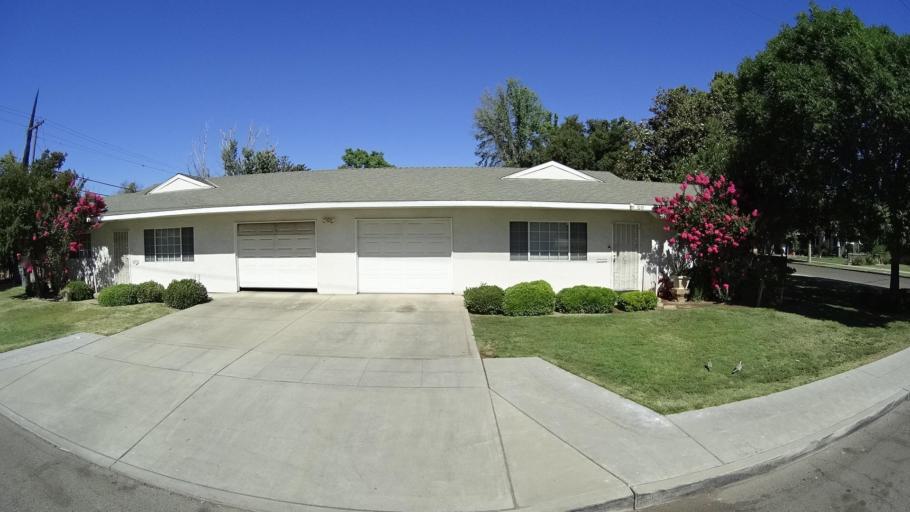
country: US
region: California
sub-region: Fresno County
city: Fresno
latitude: 36.7784
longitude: -119.7973
